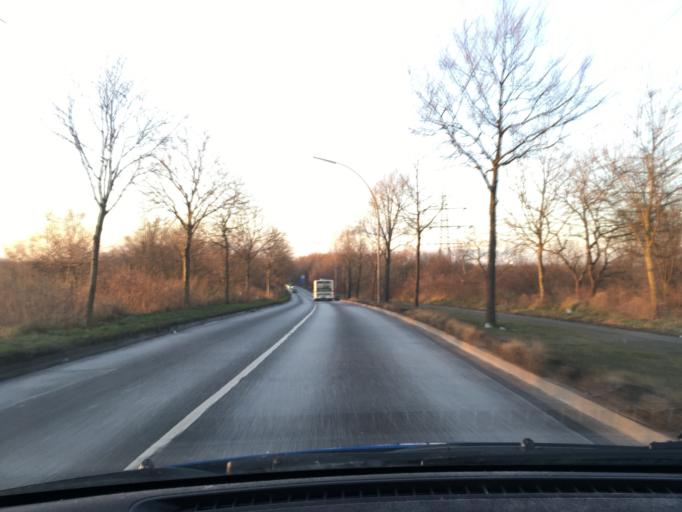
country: DE
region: Hamburg
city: Harburg
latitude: 53.4788
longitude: 9.9244
